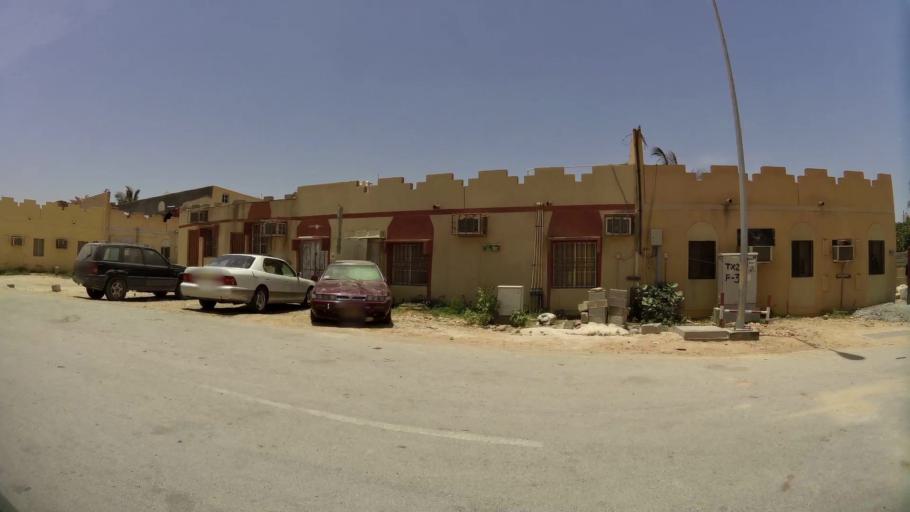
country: OM
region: Zufar
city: Salalah
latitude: 17.0820
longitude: 54.1521
